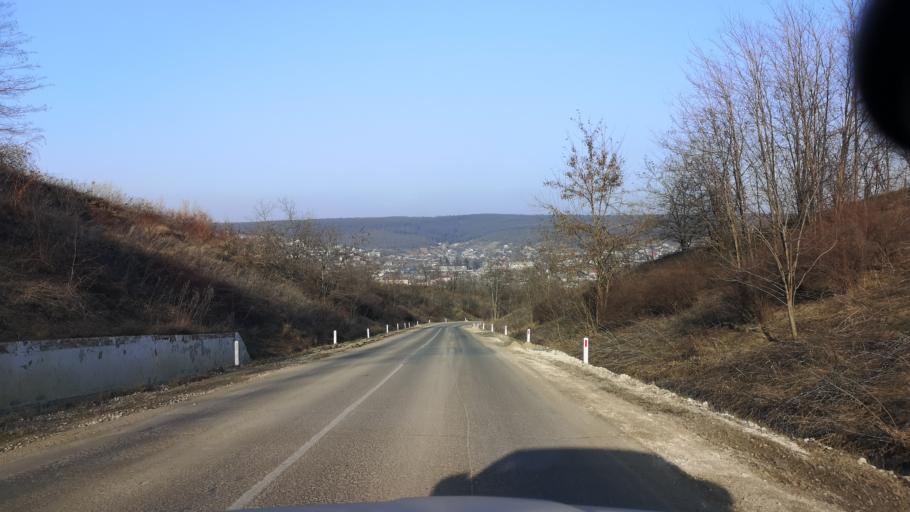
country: MD
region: Stinga Nistrului
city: Bucovat
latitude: 47.1072
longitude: 28.4987
